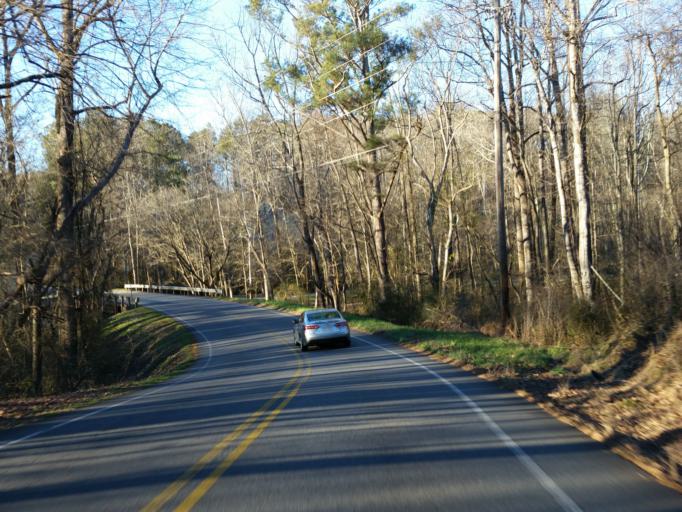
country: US
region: Georgia
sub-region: Cherokee County
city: Holly Springs
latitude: 34.1366
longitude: -84.4526
